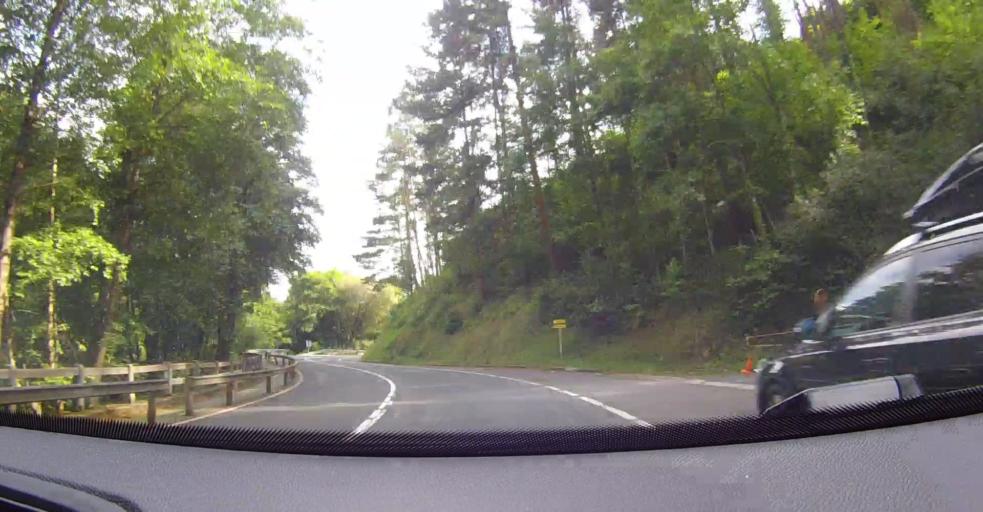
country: ES
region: Basque Country
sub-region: Bizkaia
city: Elantxobe
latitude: 43.4007
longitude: -2.6474
